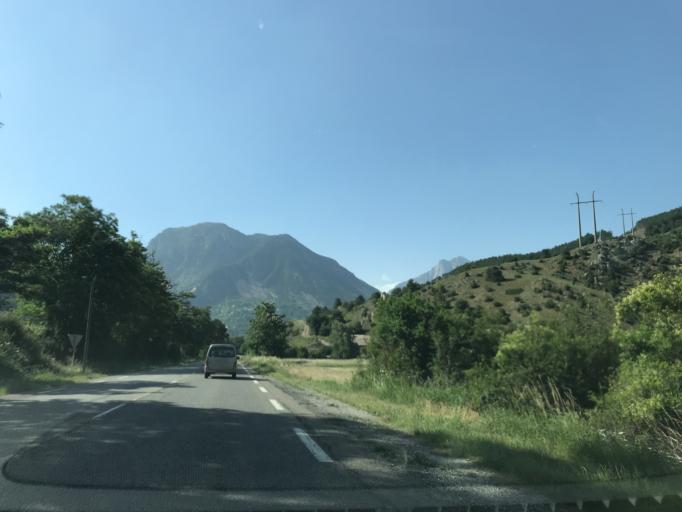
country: FR
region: Provence-Alpes-Cote d'Azur
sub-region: Departement des Hautes-Alpes
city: Saint-Martin-de-Queyrieres
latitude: 44.7660
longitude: 6.5657
